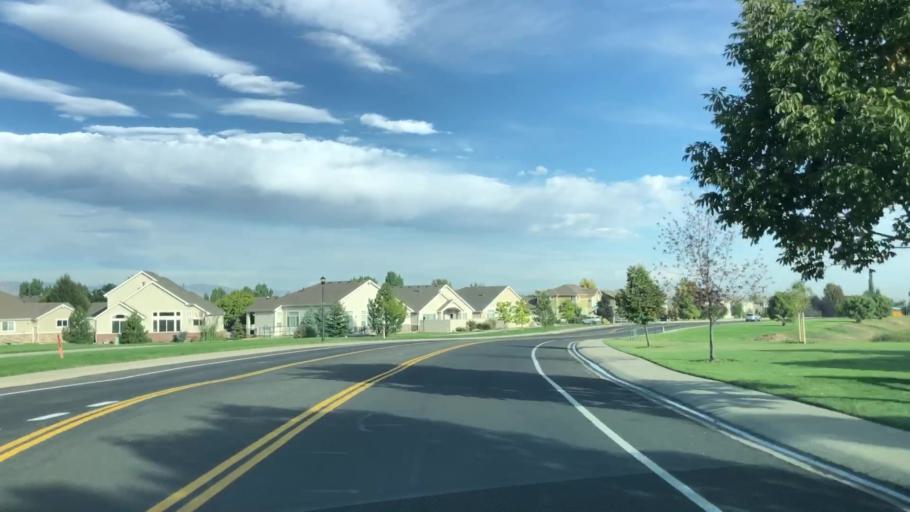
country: US
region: Colorado
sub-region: Weld County
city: Windsor
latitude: 40.4694
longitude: -104.9787
